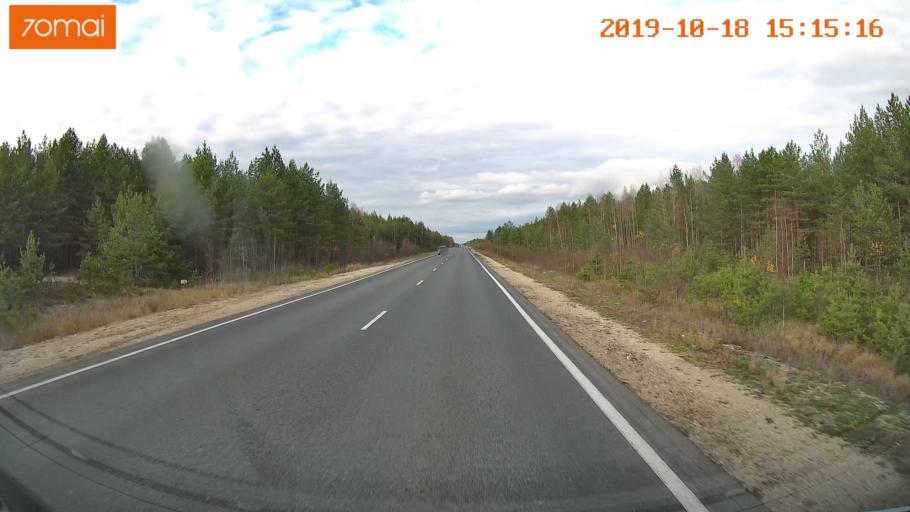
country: RU
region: Vladimir
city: Gus'-Khrustal'nyy
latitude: 55.6162
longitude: 40.7221
